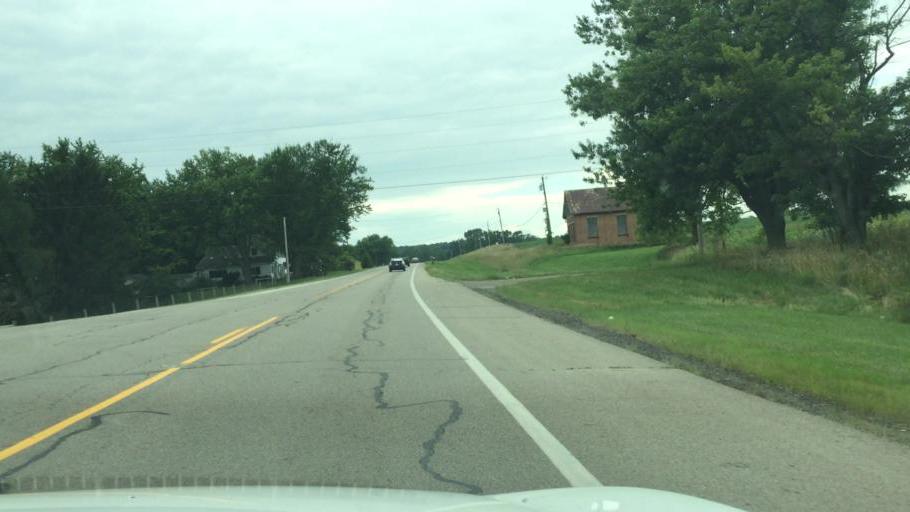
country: US
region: Ohio
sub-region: Champaign County
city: Mechanicsburg
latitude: 40.0763
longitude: -83.5705
